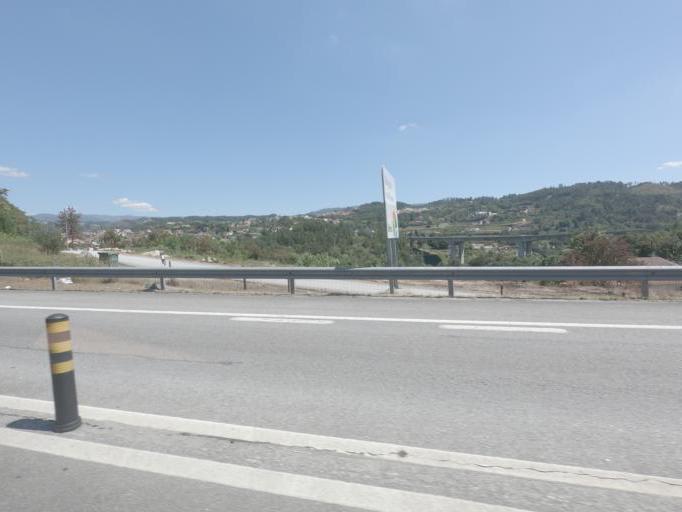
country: PT
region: Porto
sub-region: Amarante
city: Amarante
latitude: 41.2625
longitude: -8.0952
